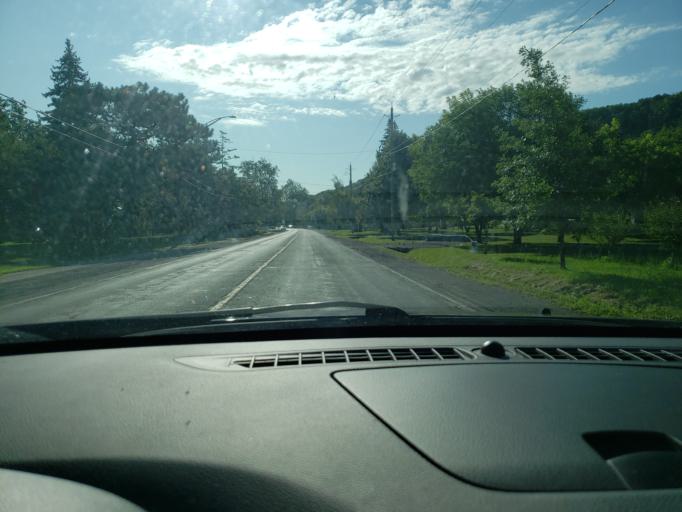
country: CA
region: Ontario
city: Hamilton
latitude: 43.1953
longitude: -79.6010
